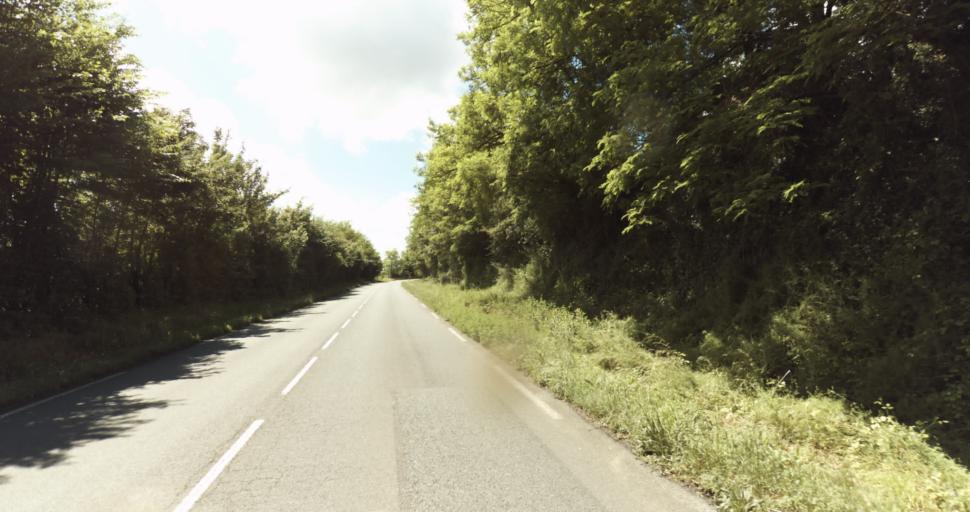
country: FR
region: Aquitaine
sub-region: Departement de la Dordogne
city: Beaumont-du-Perigord
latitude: 44.7799
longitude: 0.7670
